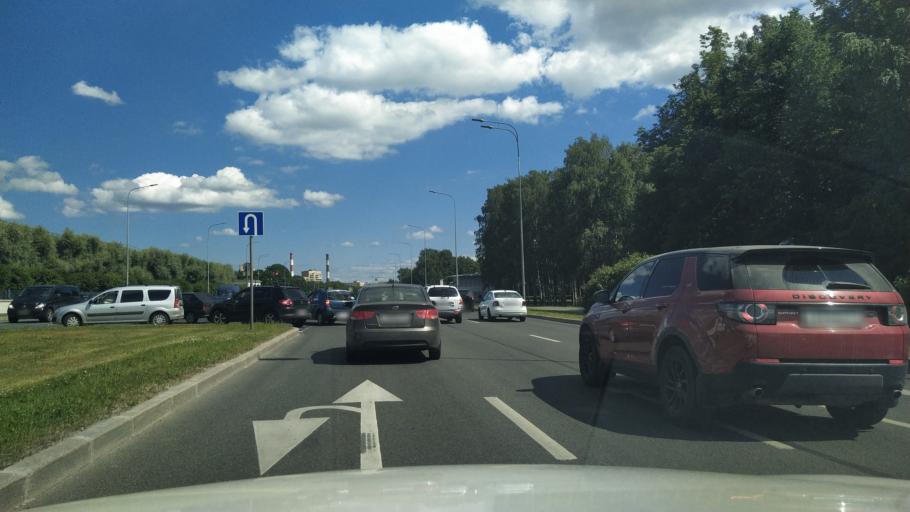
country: RU
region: Leningrad
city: Kalininskiy
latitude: 59.9943
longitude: 30.4157
